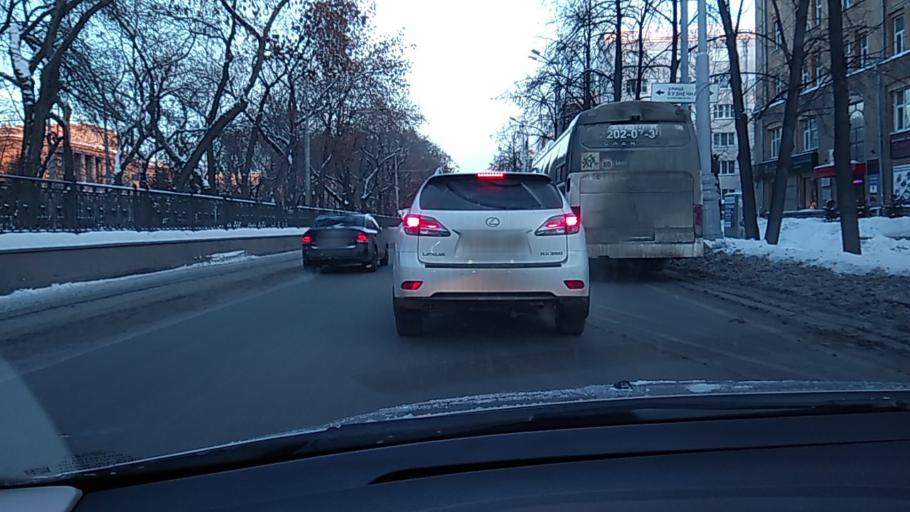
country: RU
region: Sverdlovsk
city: Yekaterinburg
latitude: 56.8403
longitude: 60.6222
